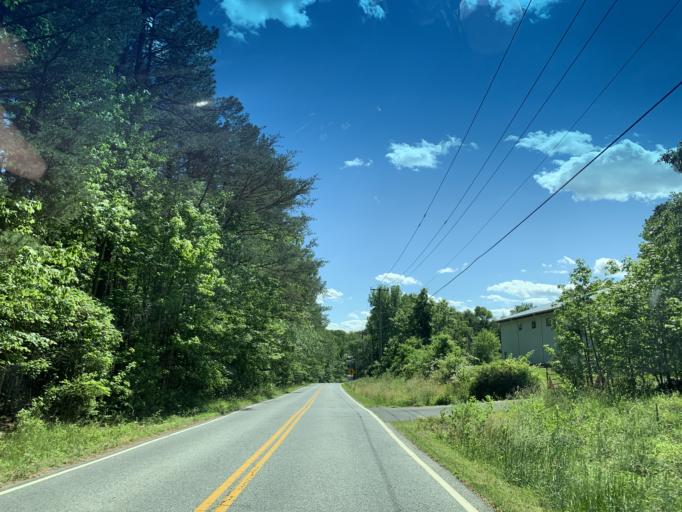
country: US
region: Maryland
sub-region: Cecil County
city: North East
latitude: 39.5435
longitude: -75.9147
